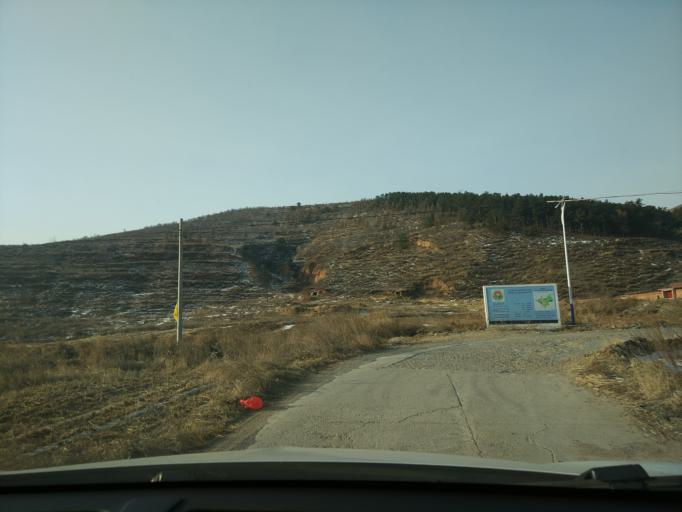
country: CN
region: Hebei
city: Xiwanzi
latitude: 40.8297
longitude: 115.5304
